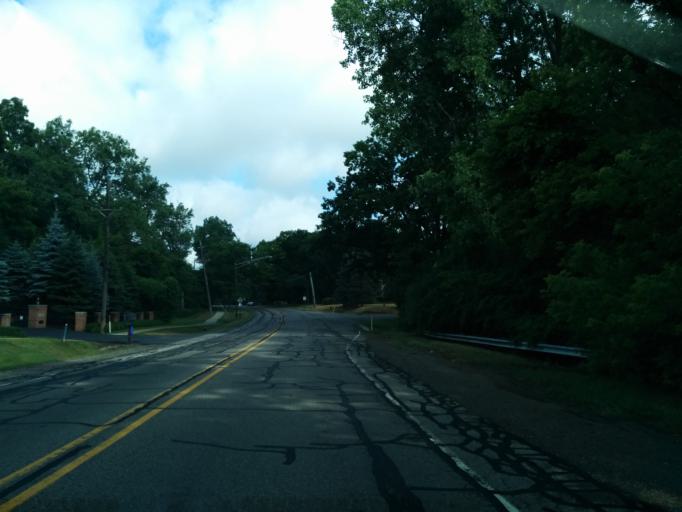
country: US
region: Michigan
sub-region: Oakland County
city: Franklin
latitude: 42.5281
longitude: -83.3298
